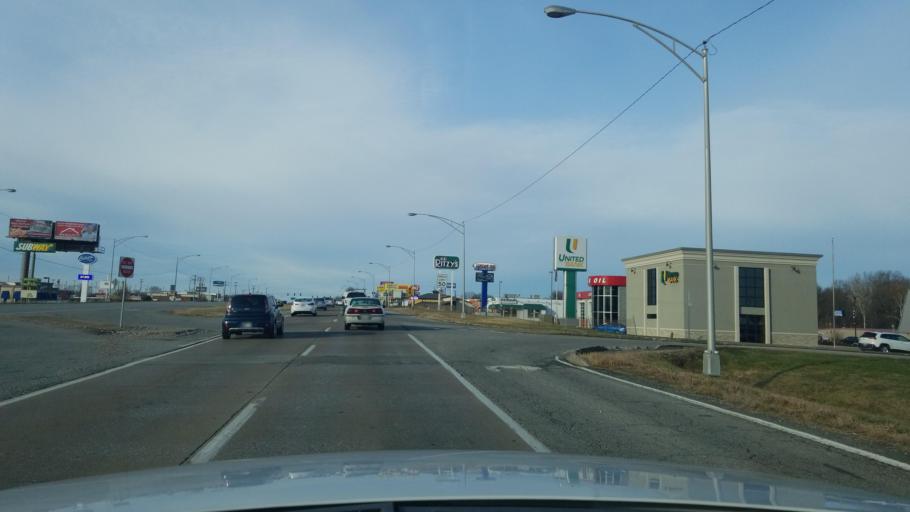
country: US
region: Indiana
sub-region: Vanderburgh County
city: Evansville
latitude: 37.9775
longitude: -87.6321
